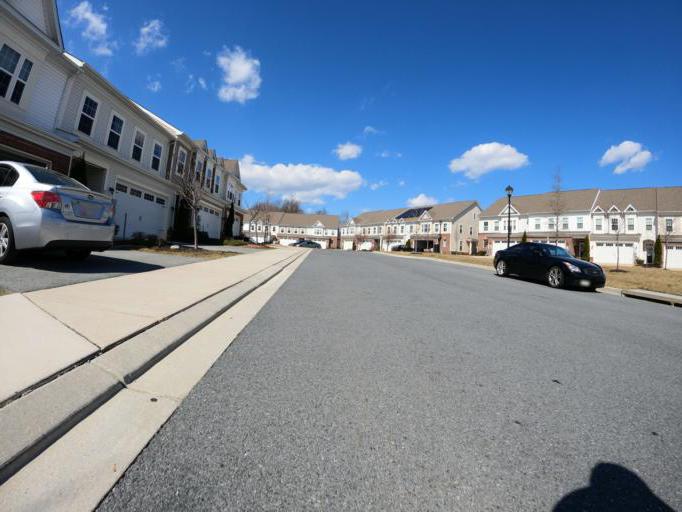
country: US
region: Maryland
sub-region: Howard County
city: Ellicott City
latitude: 39.2887
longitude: -76.8238
